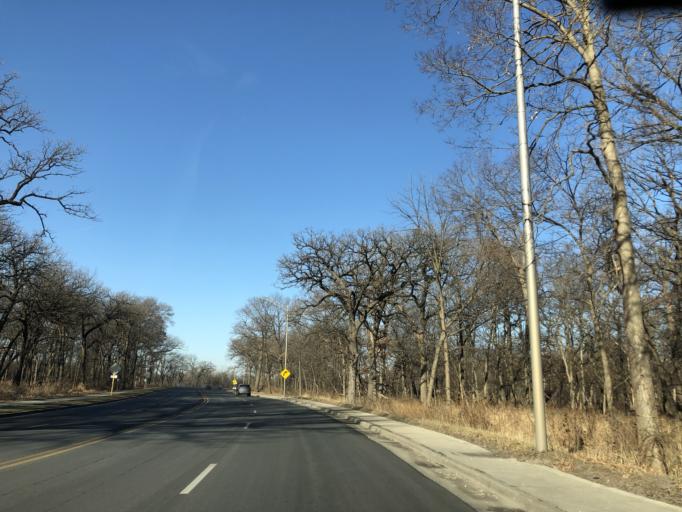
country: US
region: Illinois
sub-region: Cook County
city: Riverside
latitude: 41.8365
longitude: -87.8300
